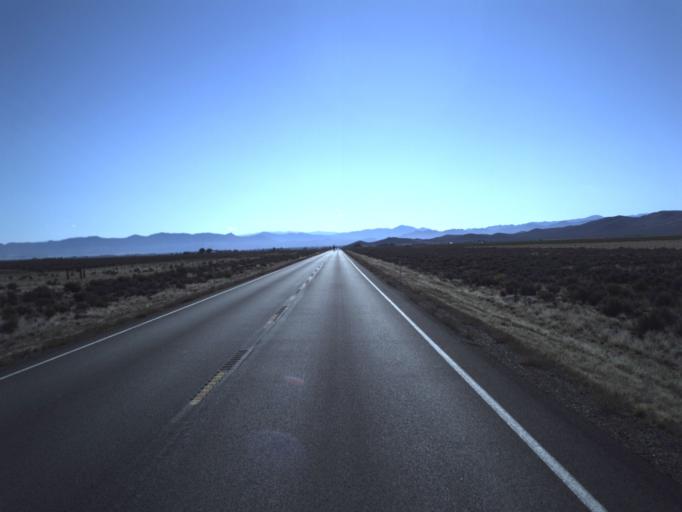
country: US
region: Utah
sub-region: Washington County
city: Enterprise
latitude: 37.7649
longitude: -113.8130
